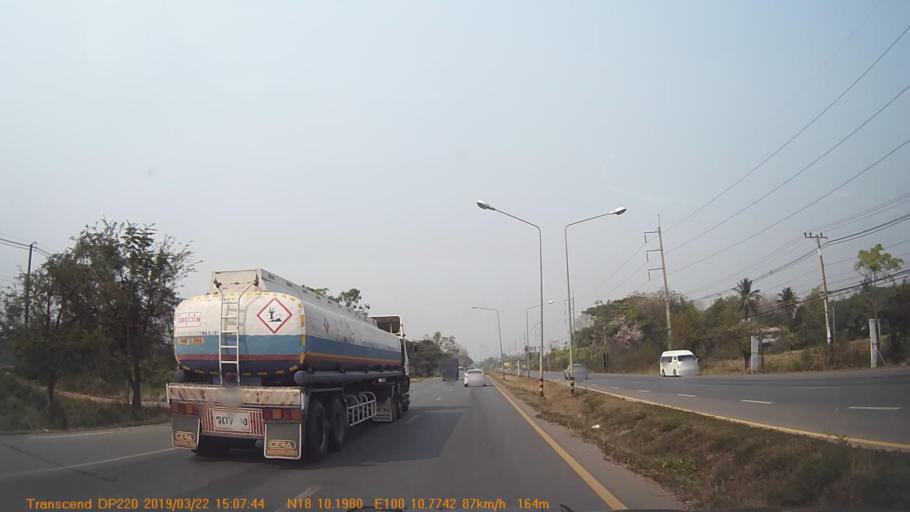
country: TH
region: Phrae
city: Phrae
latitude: 18.1702
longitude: 100.1796
